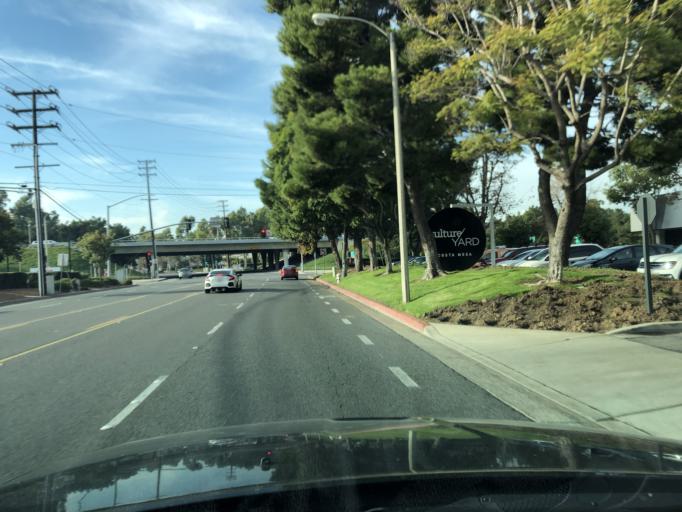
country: US
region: California
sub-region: Orange County
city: Irvine
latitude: 33.6813
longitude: -117.8761
